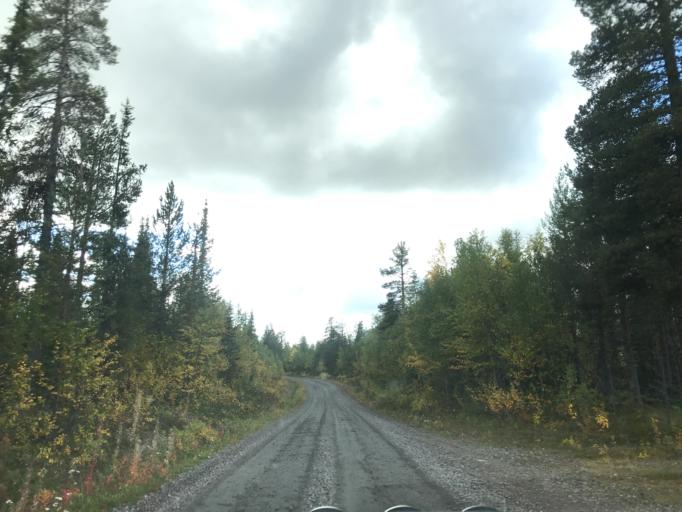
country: SE
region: Norrbotten
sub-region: Gallivare Kommun
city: Malmberget
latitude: 67.5929
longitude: 20.8809
